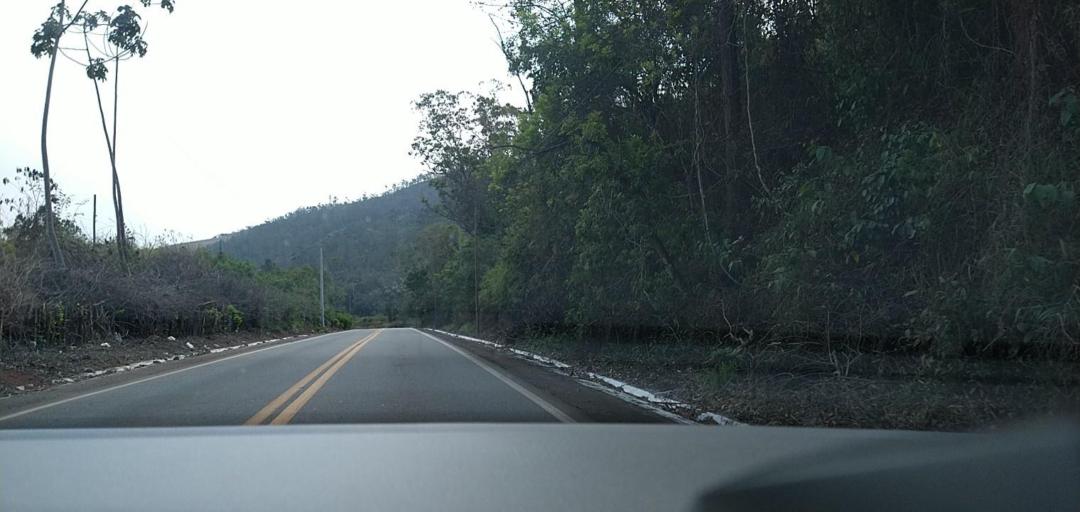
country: BR
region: Minas Gerais
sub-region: Rio Piracicaba
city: Rio Piracicaba
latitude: -19.8876
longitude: -43.1333
